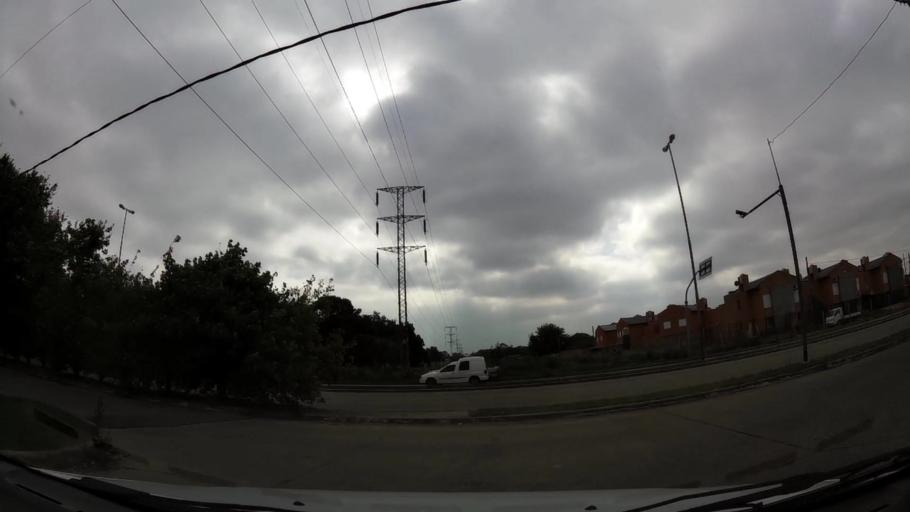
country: AR
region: Buenos Aires
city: San Justo
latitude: -34.7191
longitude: -58.5350
